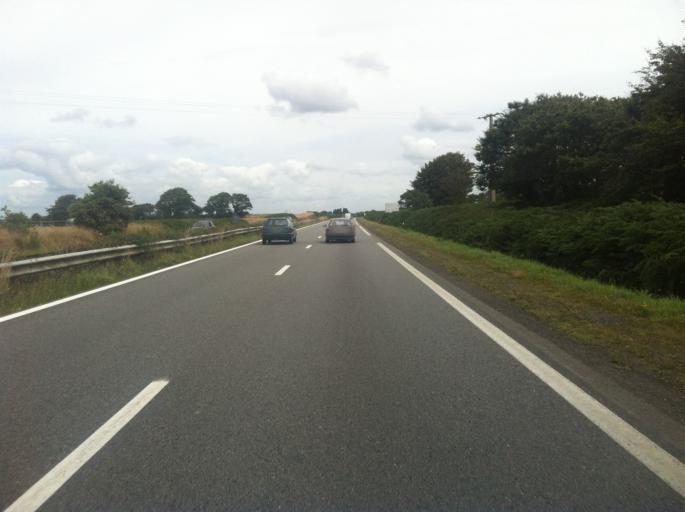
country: FR
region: Brittany
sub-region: Departement du Finistere
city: Saint-Thonan
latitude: 48.4754
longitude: -4.3179
